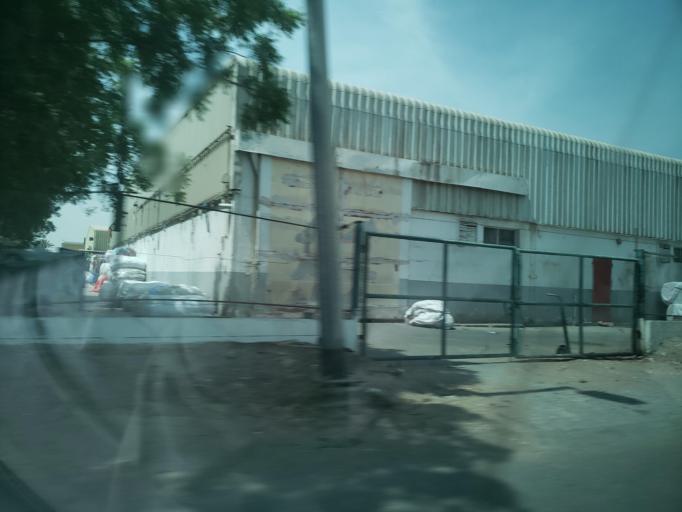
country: AE
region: Ash Shariqah
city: Sharjah
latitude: 25.3336
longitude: 55.4933
